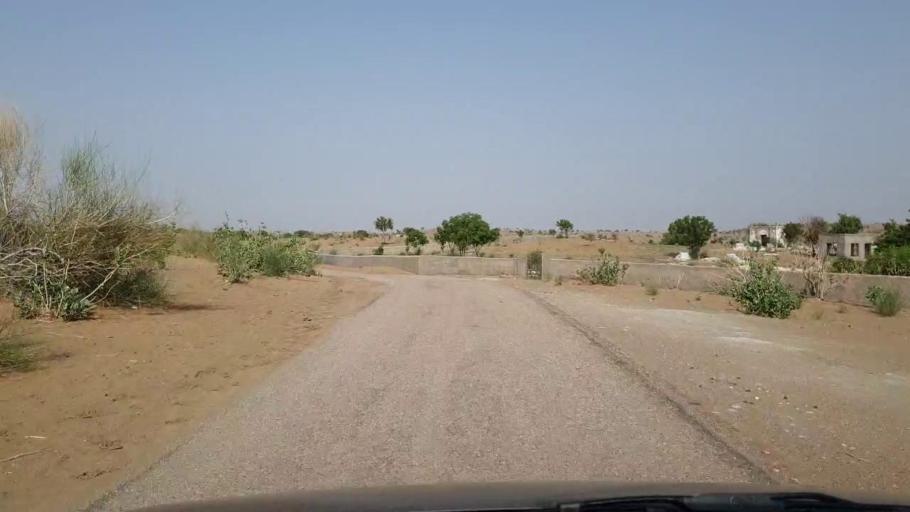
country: PK
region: Sindh
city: Chor
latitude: 25.4529
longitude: 70.5277
